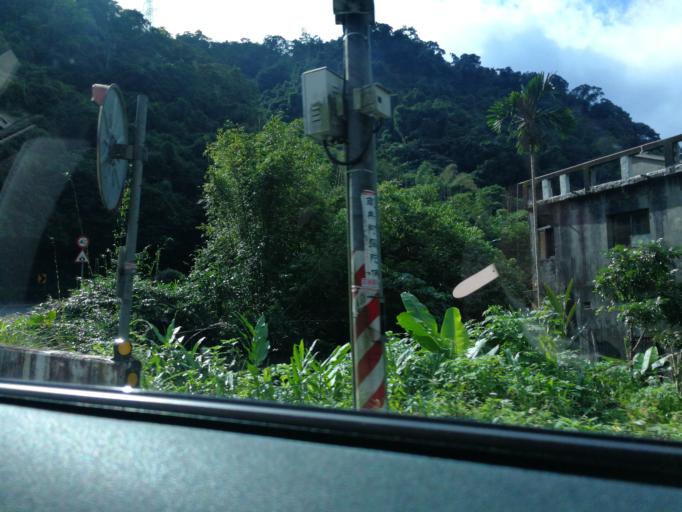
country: TW
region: Taipei
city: Taipei
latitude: 24.9565
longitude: 121.5706
